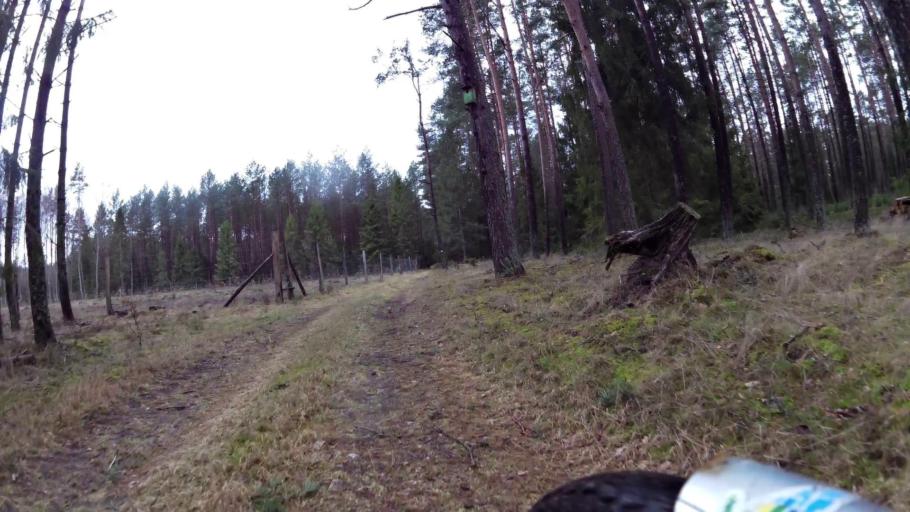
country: PL
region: Pomeranian Voivodeship
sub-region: Powiat bytowski
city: Borzytuchom
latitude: 54.2633
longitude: 17.3430
